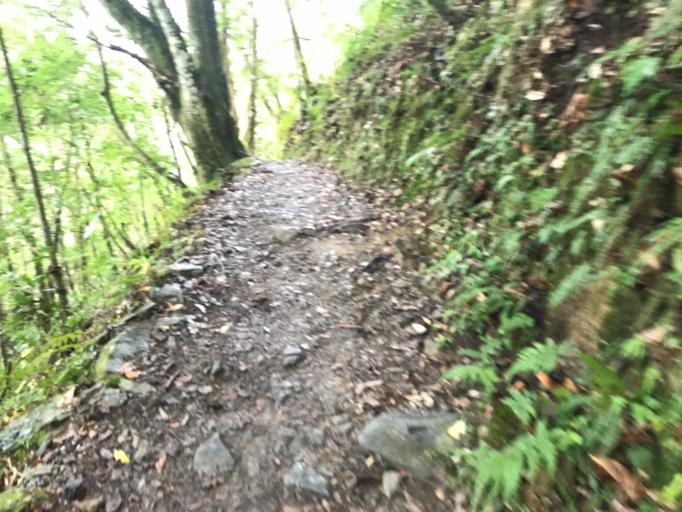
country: TW
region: Taiwan
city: Daxi
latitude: 24.5503
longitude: 121.2916
